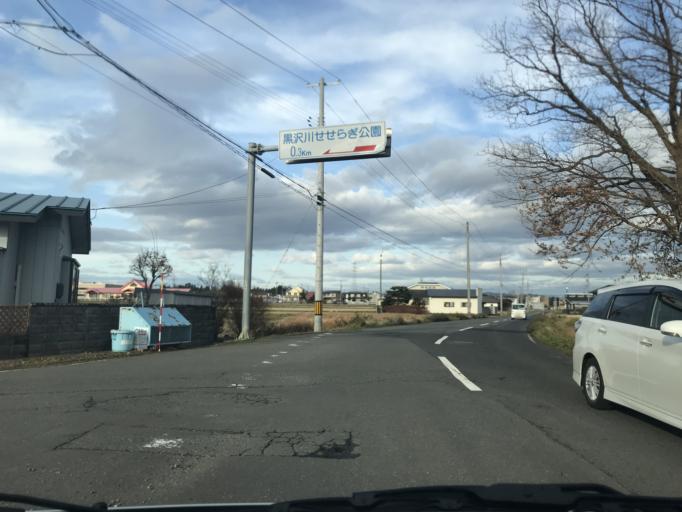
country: JP
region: Iwate
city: Mizusawa
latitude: 39.1874
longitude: 141.1062
